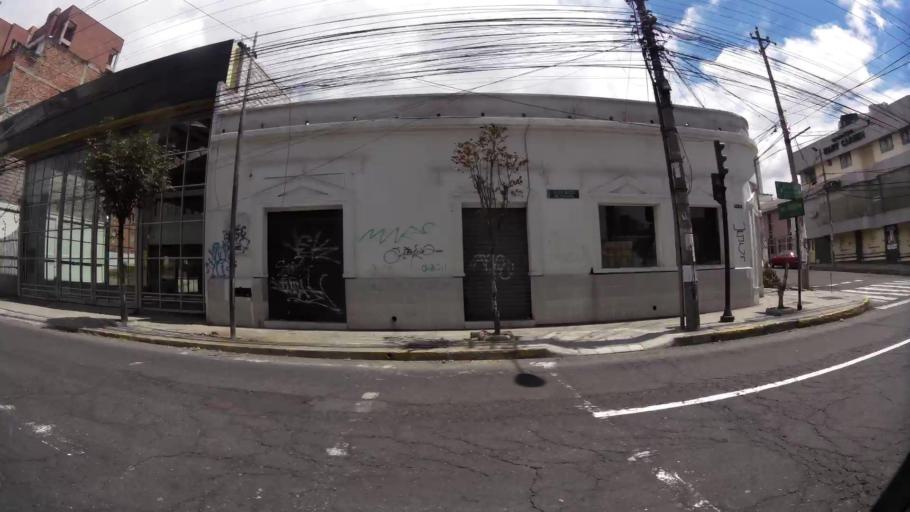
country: EC
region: Pichincha
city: Quito
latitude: -0.1856
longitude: -78.4911
